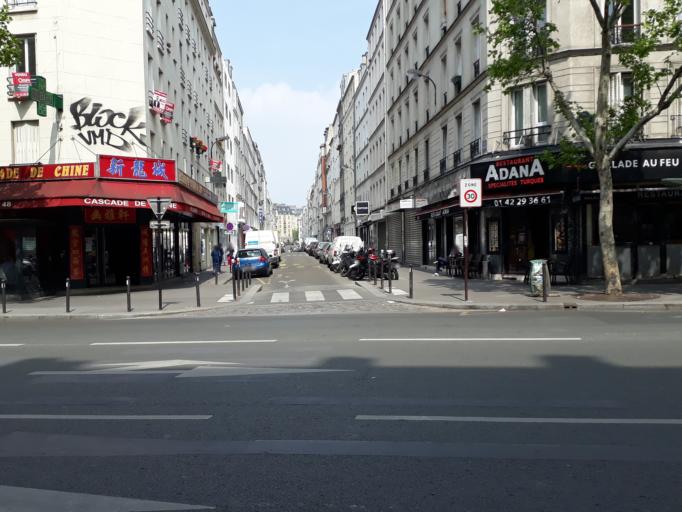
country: FR
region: Ile-de-France
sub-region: Departement des Hauts-de-Seine
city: Clichy
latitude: 48.8919
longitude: 2.3179
